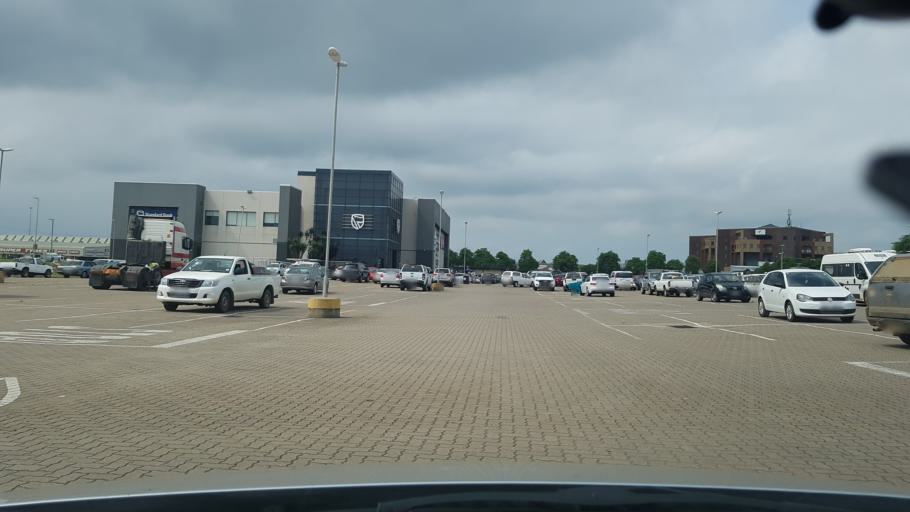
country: ZA
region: KwaZulu-Natal
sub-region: uThungulu District Municipality
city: Richards Bay
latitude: -28.7550
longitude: 32.0471
